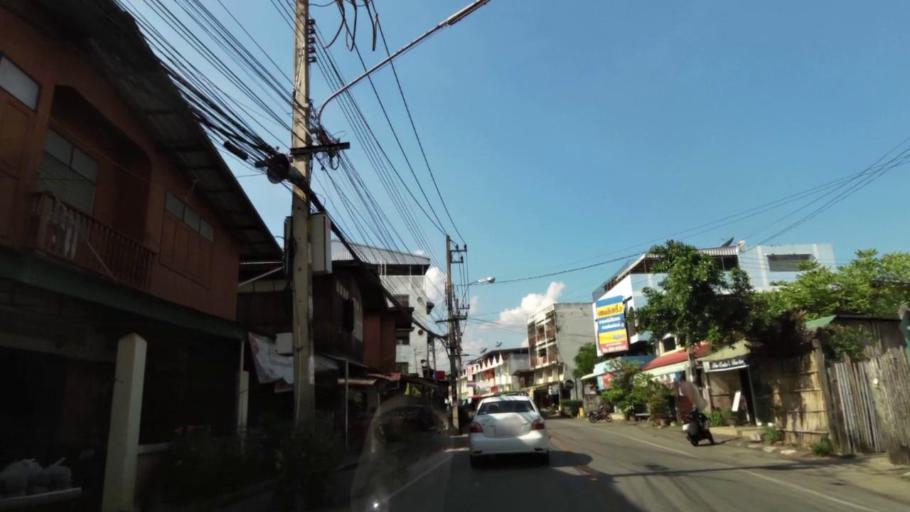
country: TH
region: Phrae
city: Phrae
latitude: 18.1375
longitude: 100.1455
